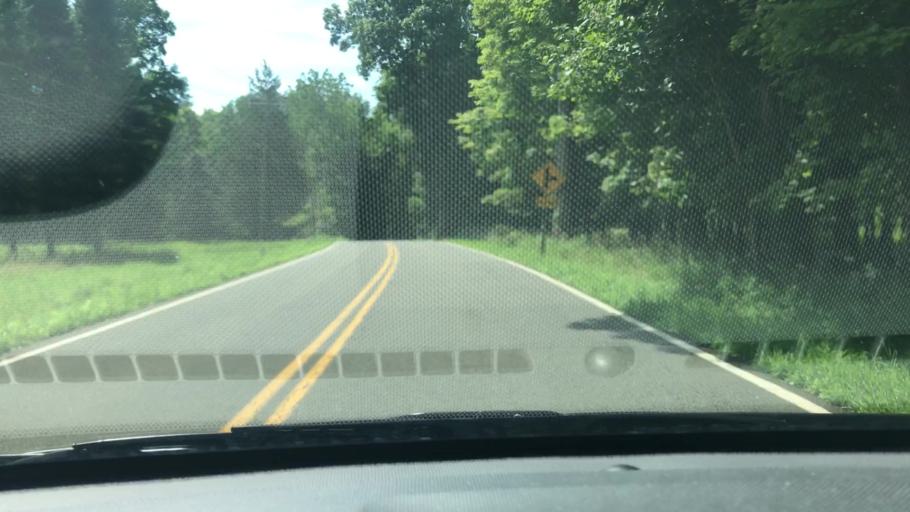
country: US
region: New York
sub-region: Ulster County
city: Shokan
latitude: 41.9233
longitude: -74.2147
